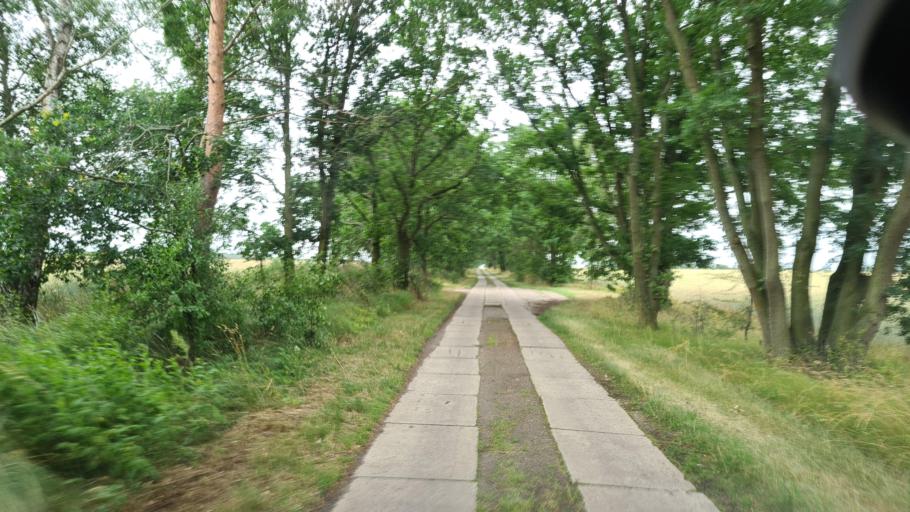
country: DE
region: Brandenburg
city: Juterbog
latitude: 51.9674
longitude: 13.1706
